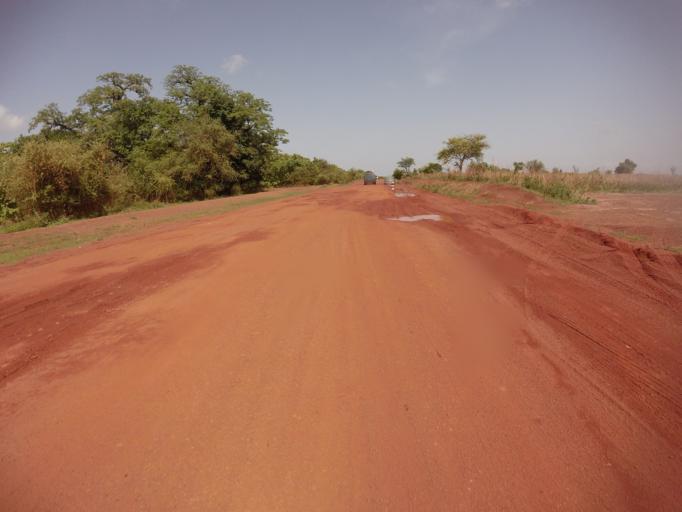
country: GH
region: Upper East
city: Bawku
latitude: 11.0029
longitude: -0.1974
